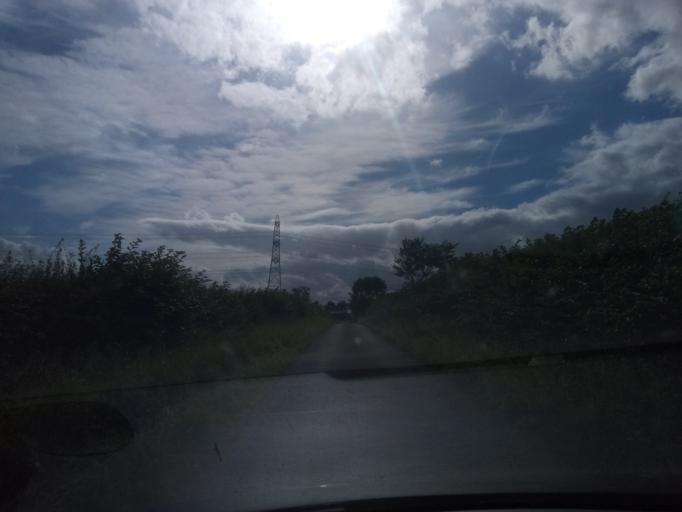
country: GB
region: Scotland
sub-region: The Scottish Borders
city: Coldstream
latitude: 55.6267
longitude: -2.1847
